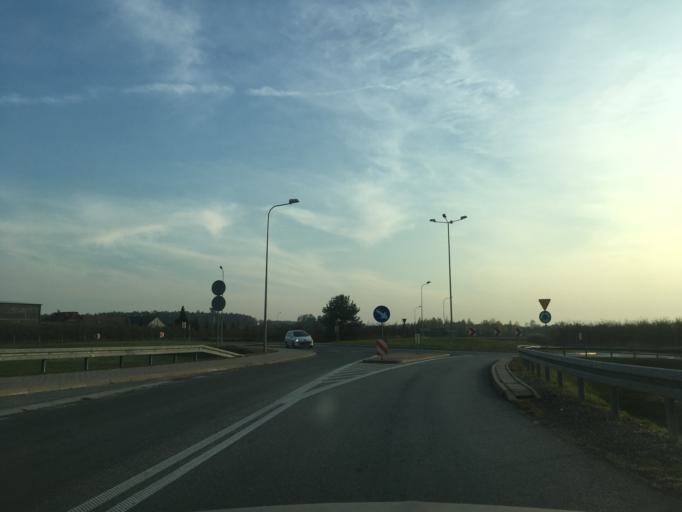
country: PL
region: Lodz Voivodeship
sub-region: Powiat skierniewicki
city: Kowiesy
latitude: 51.9178
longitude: 20.4564
